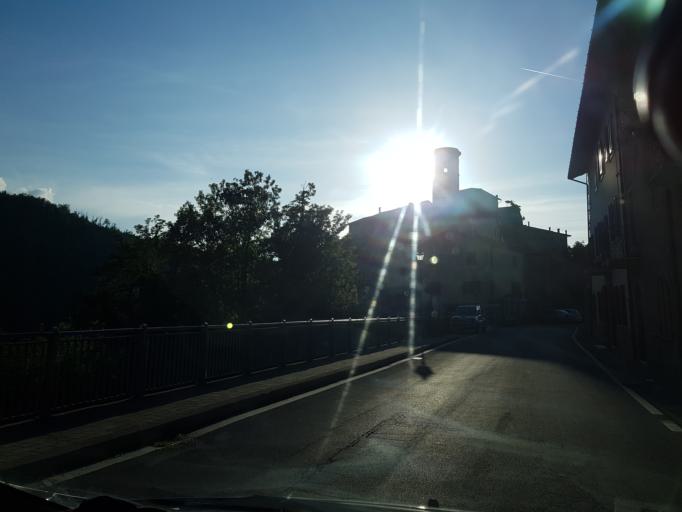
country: IT
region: Tuscany
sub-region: Provincia di Lucca
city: Minucciano
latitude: 44.1701
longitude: 10.2094
